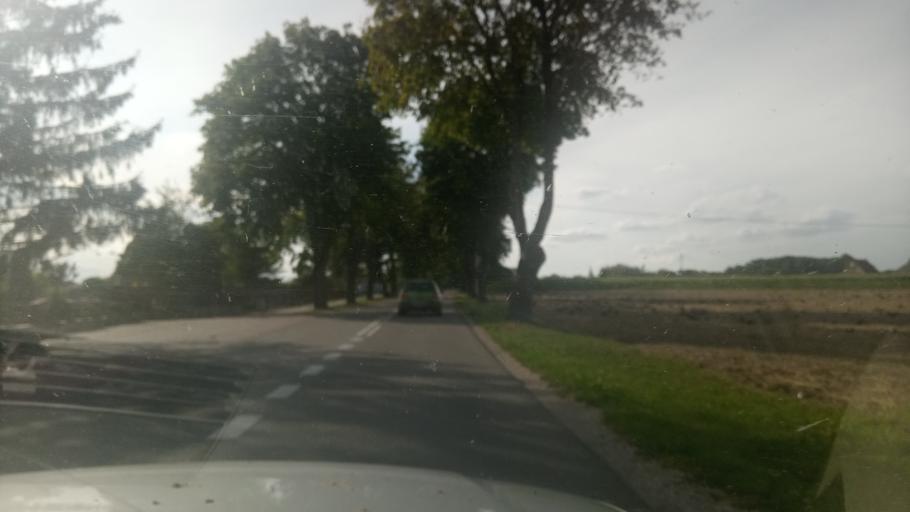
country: PL
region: Greater Poland Voivodeship
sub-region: Powiat pilski
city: Lobzenica
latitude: 53.2537
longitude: 17.2684
